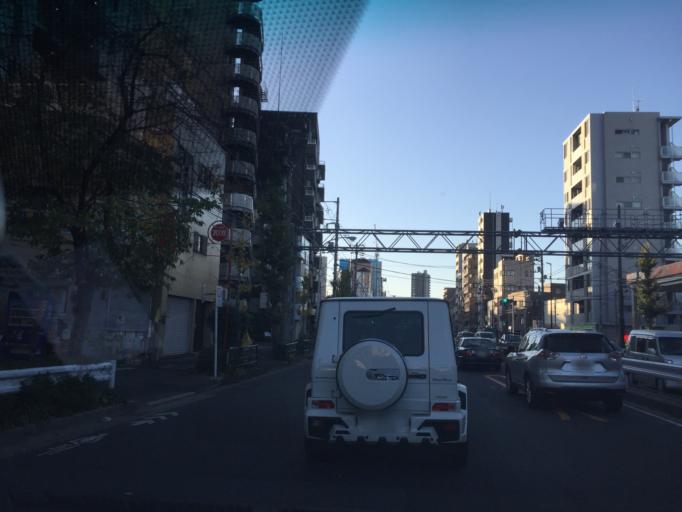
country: JP
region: Saitama
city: Kawaguchi
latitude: 35.7822
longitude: 139.7278
